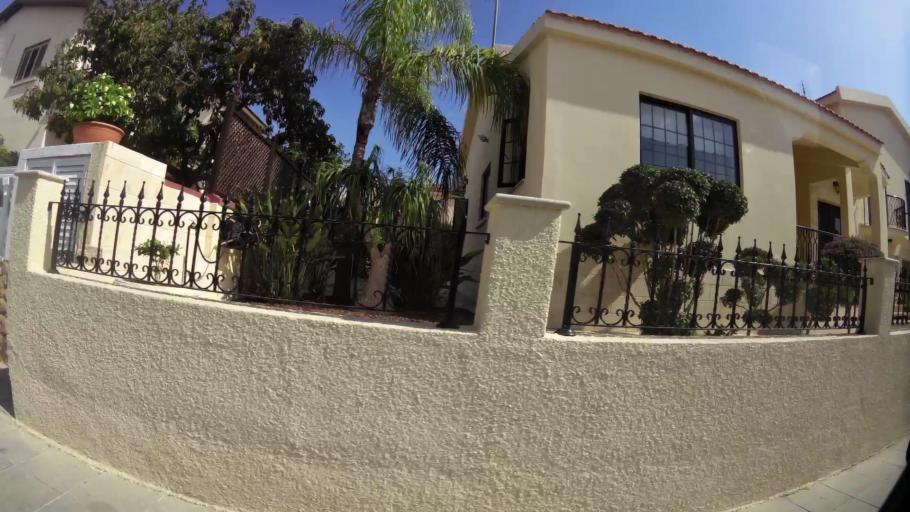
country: CY
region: Larnaka
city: Aradippou
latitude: 34.9416
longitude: 33.5879
